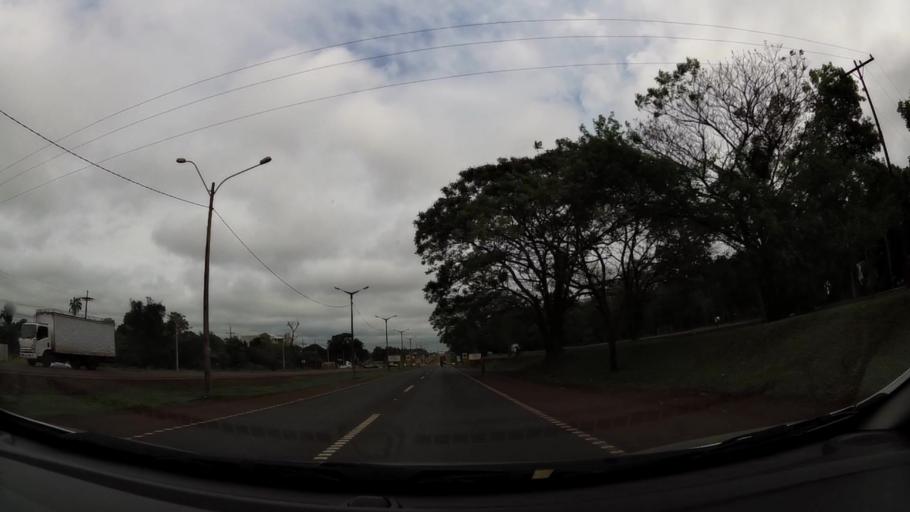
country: PY
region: Alto Parana
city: Ciudad del Este
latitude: -25.4951
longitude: -54.6950
